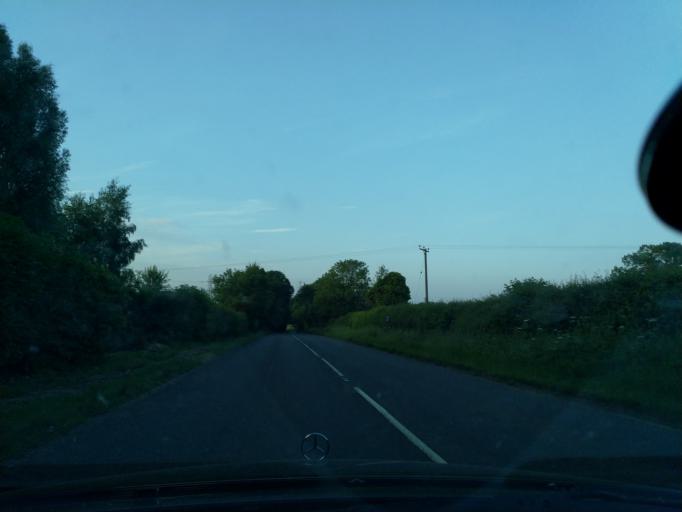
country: GB
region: England
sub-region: Solihull
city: Balsall Common
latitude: 52.3699
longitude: -1.6380
